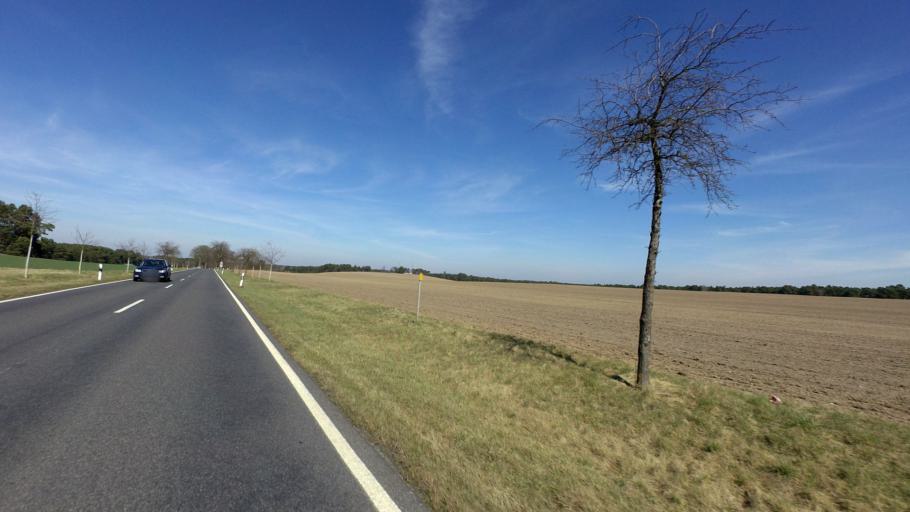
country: DE
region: Brandenburg
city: Storkow
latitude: 52.1828
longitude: 13.9183
